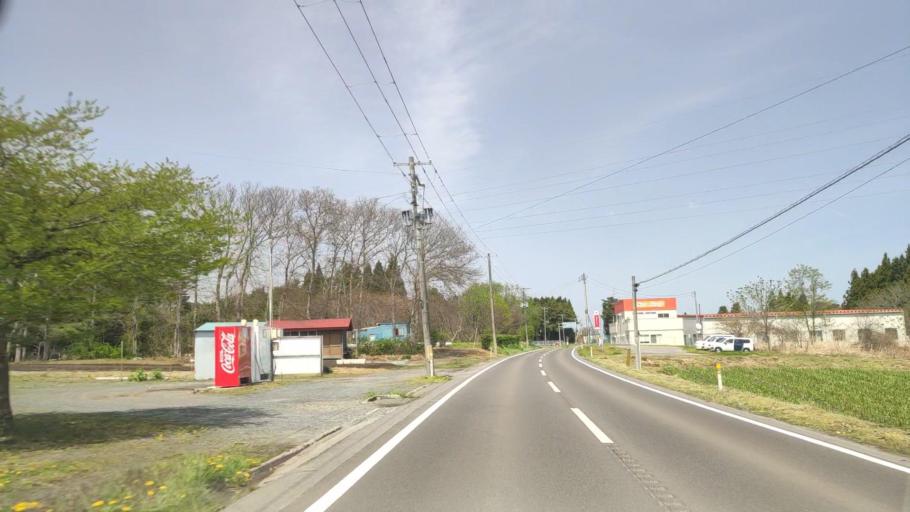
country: JP
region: Aomori
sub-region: Hachinohe Shi
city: Uchimaru
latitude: 40.5335
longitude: 141.4028
